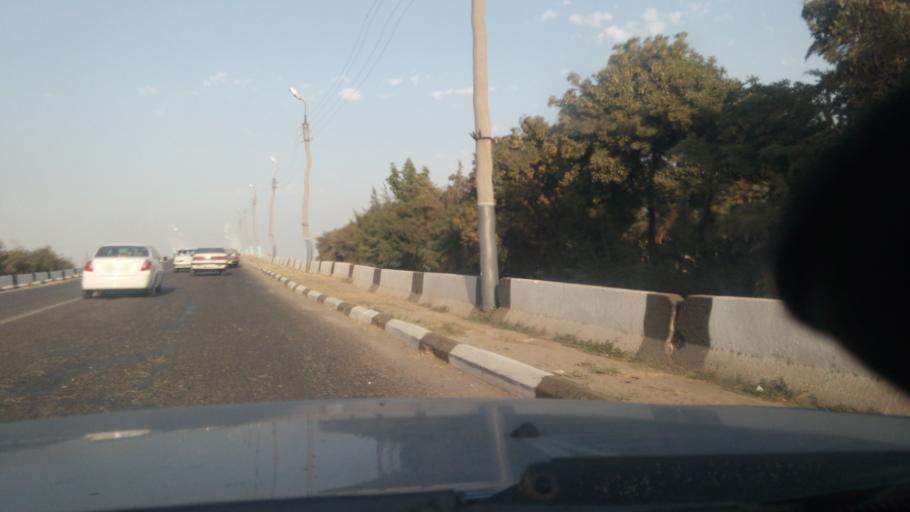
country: UZ
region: Sirdaryo
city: Guliston
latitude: 40.4737
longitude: 68.7677
